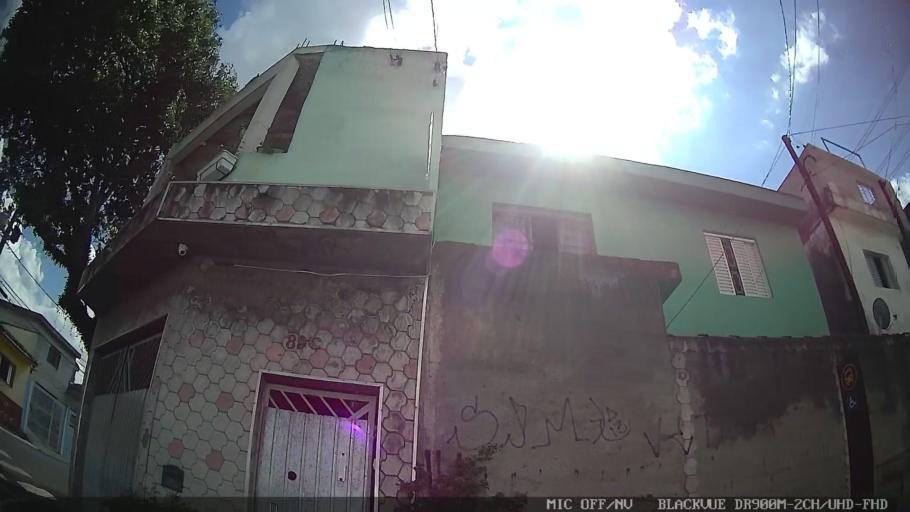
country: BR
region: Sao Paulo
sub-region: Guarulhos
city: Guarulhos
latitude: -23.5179
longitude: -46.5002
